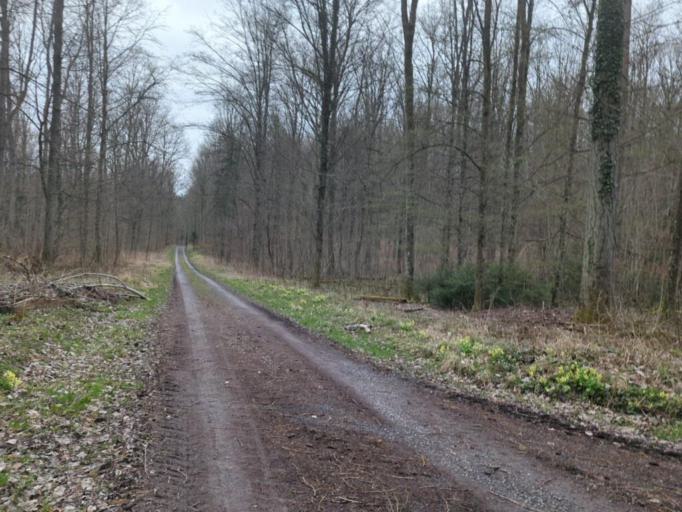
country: DE
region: Baden-Wuerttemberg
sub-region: Karlsruhe Region
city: Woessingen
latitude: 49.0334
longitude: 8.6308
